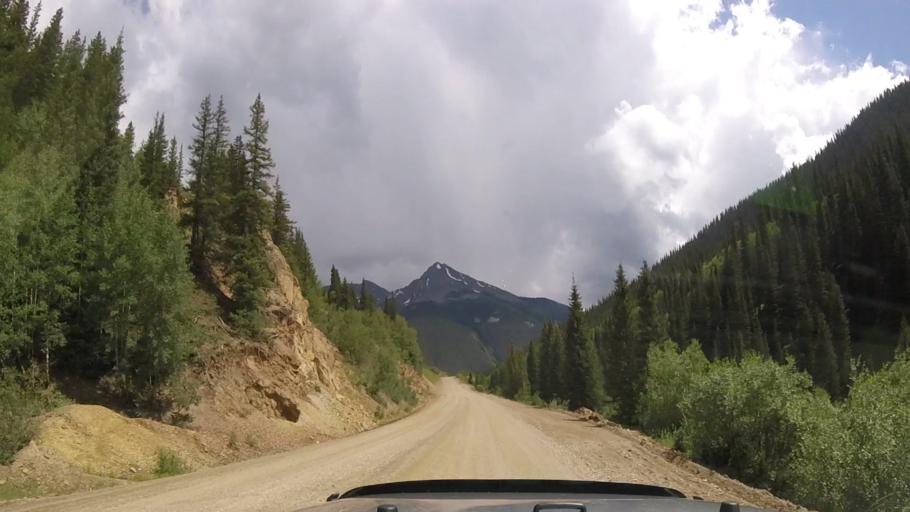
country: US
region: Colorado
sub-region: San Juan County
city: Silverton
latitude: 37.8258
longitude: -107.6676
